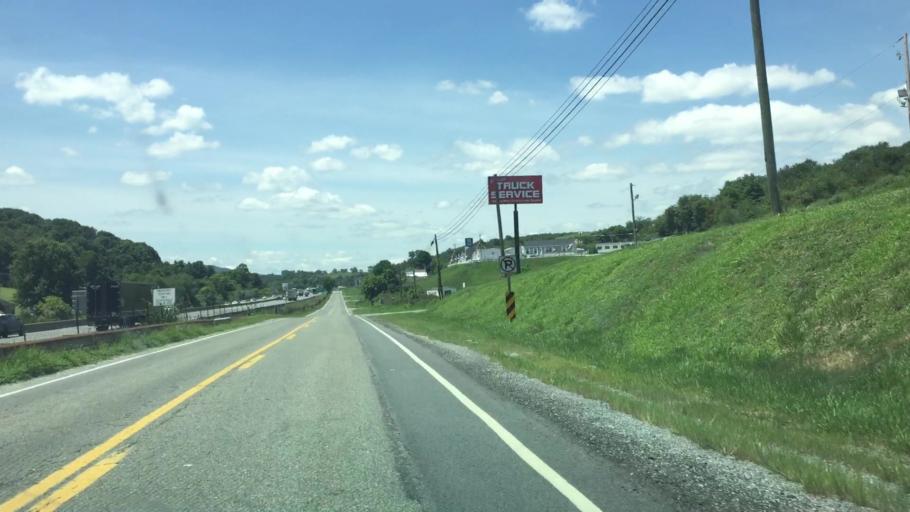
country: US
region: Virginia
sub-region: Wythe County
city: Wytheville
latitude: 36.9443
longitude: -80.9593
